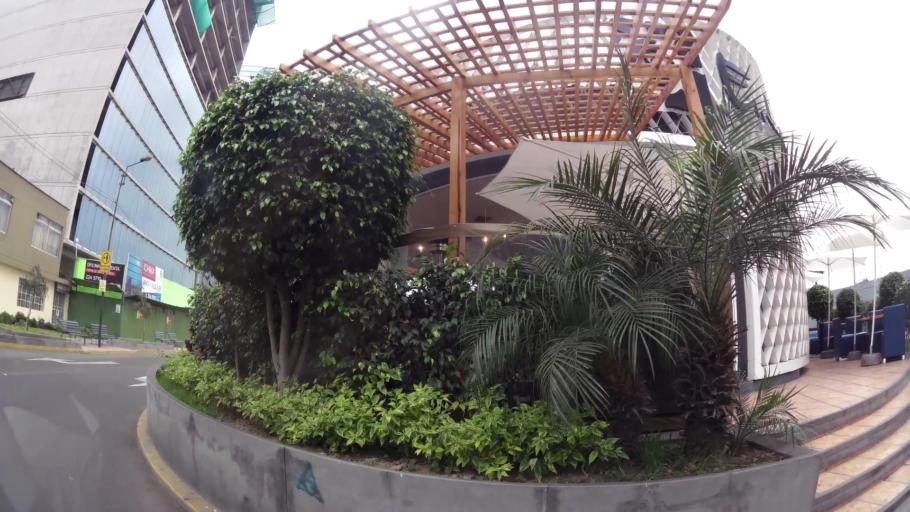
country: PE
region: Lima
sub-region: Lima
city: San Luis
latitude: -12.0970
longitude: -77.0217
